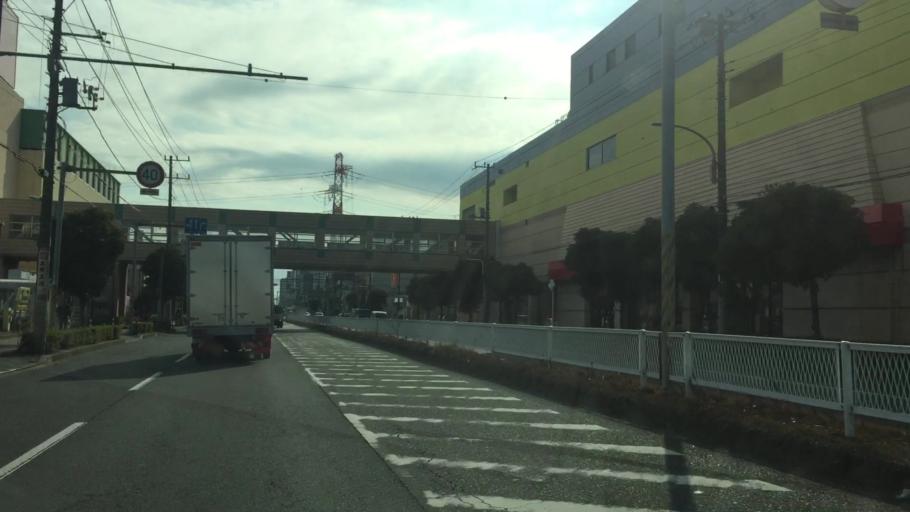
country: JP
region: Tokyo
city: Urayasu
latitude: 35.6687
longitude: 139.9043
